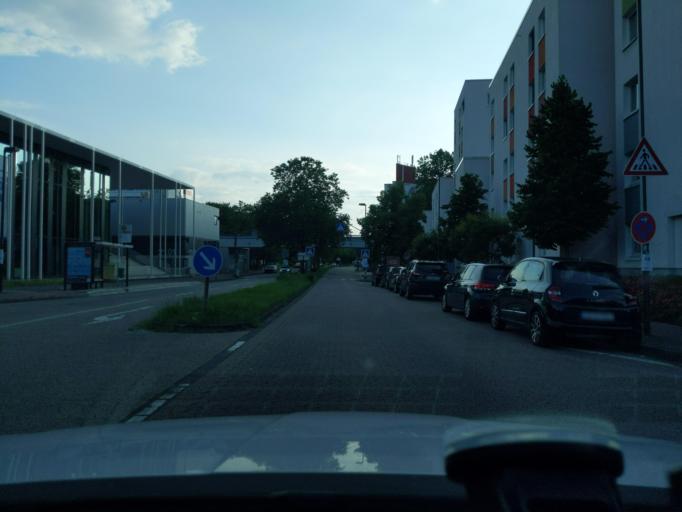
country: DE
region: North Rhine-Westphalia
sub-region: Regierungsbezirk Dusseldorf
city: Dusseldorf
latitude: 51.1919
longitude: 6.7944
